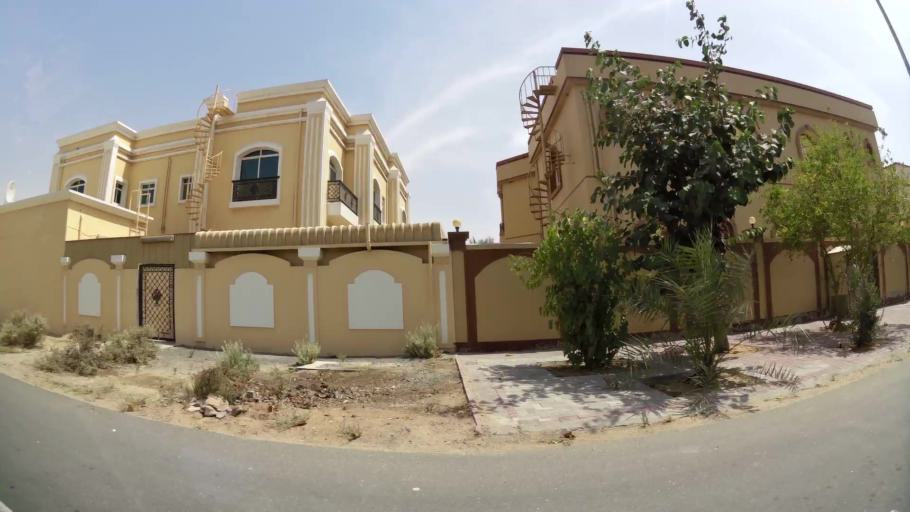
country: AE
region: Ash Shariqah
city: Sharjah
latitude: 25.2429
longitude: 55.4268
